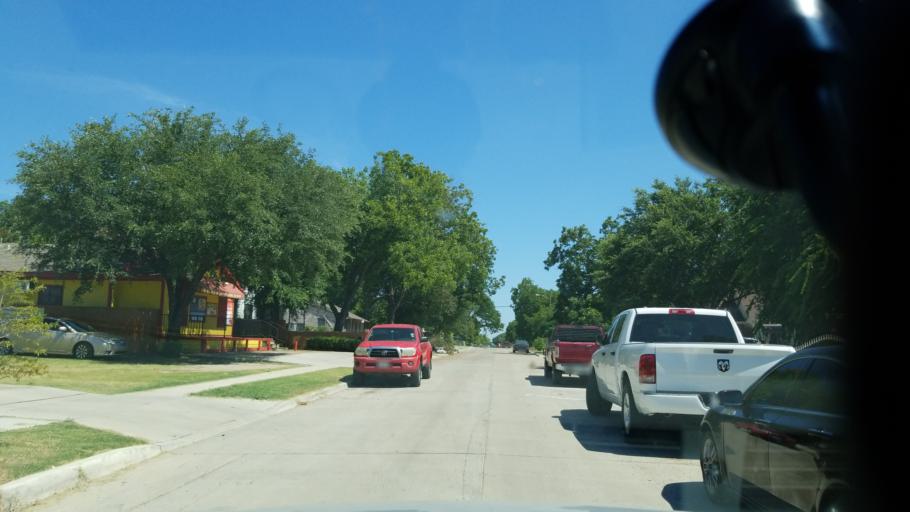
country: US
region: Texas
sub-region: Dallas County
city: Cockrell Hill
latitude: 32.7084
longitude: -96.8182
